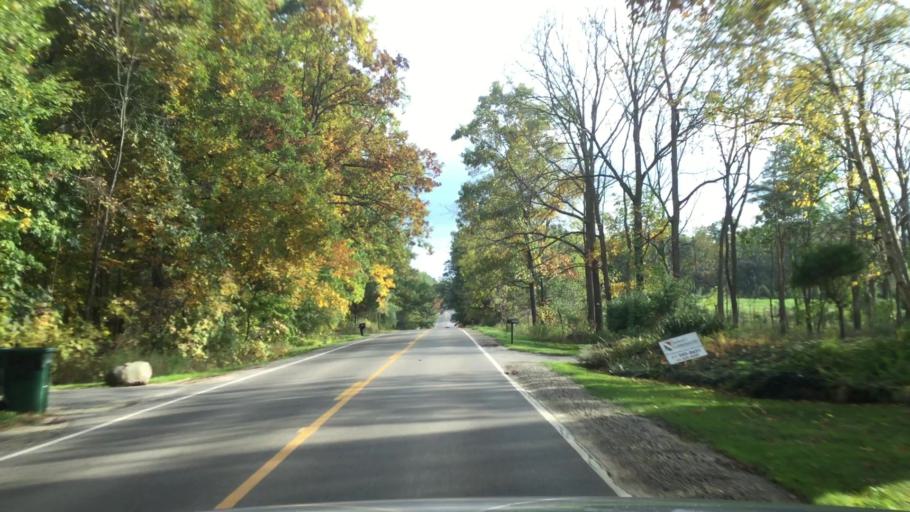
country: US
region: Michigan
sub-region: Oakland County
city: Milford
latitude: 42.6680
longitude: -83.7015
